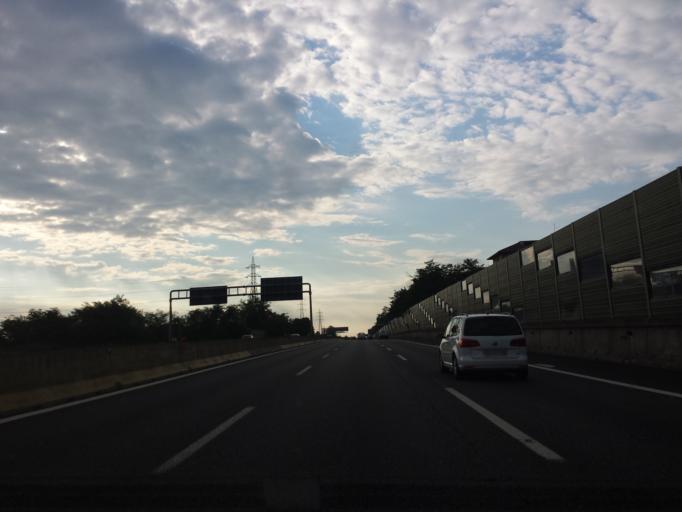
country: IT
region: Lombardy
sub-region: Citta metropolitana di Milano
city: Rescaldina
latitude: 45.6074
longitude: 8.9348
